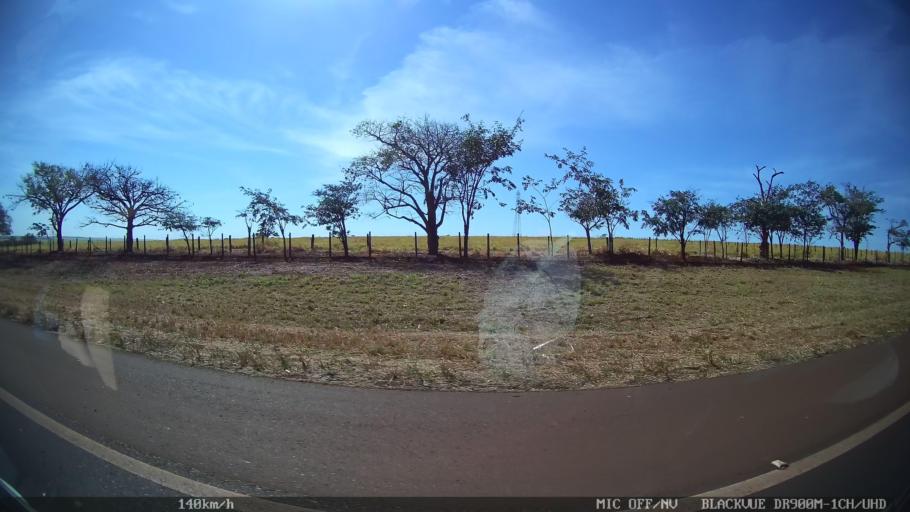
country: BR
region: Sao Paulo
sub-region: Ipua
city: Ipua
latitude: -20.4724
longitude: -48.1043
